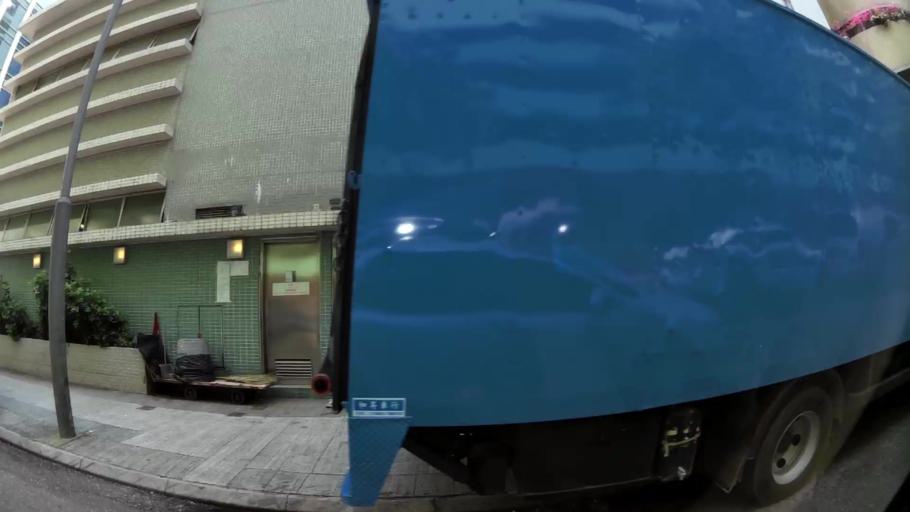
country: HK
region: Sham Shui Po
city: Sham Shui Po
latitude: 22.3337
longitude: 114.1525
